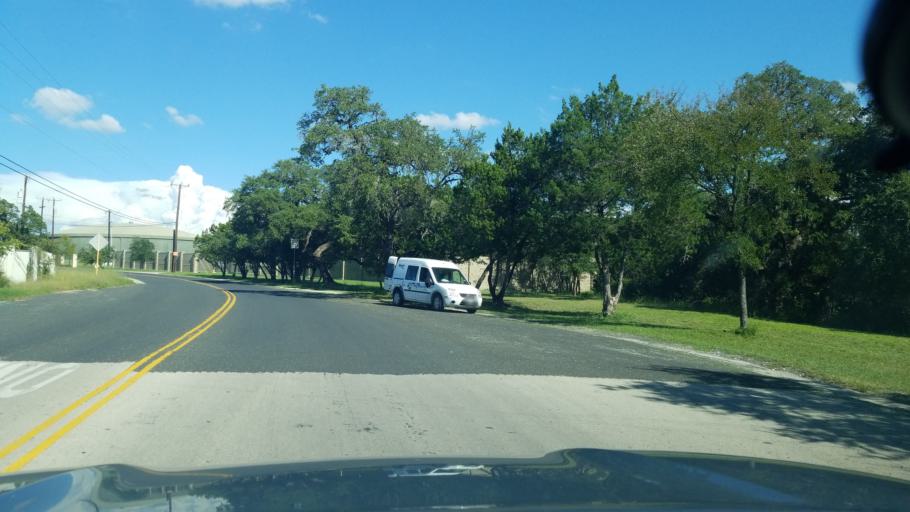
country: US
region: Texas
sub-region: Bexar County
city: Timberwood Park
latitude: 29.6660
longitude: -98.5194
